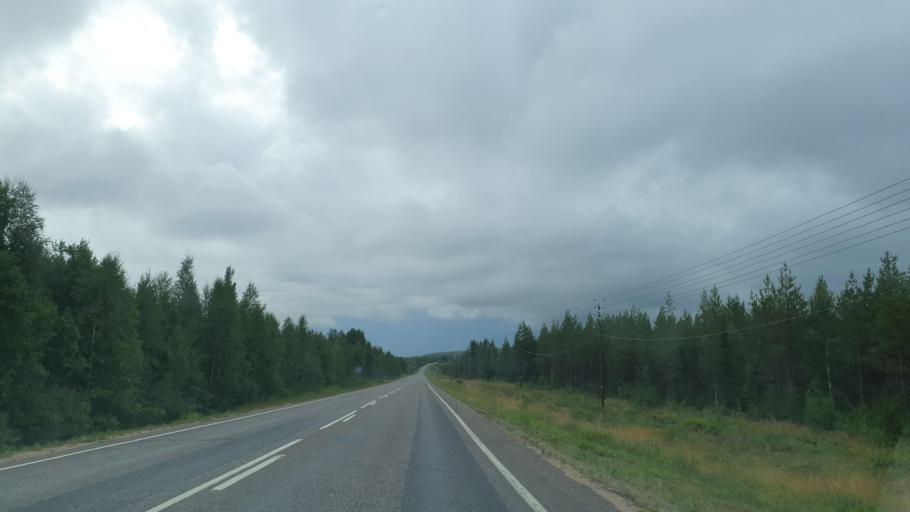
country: FI
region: Lapland
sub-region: Tunturi-Lappi
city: Kolari
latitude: 67.2056
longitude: 23.9092
